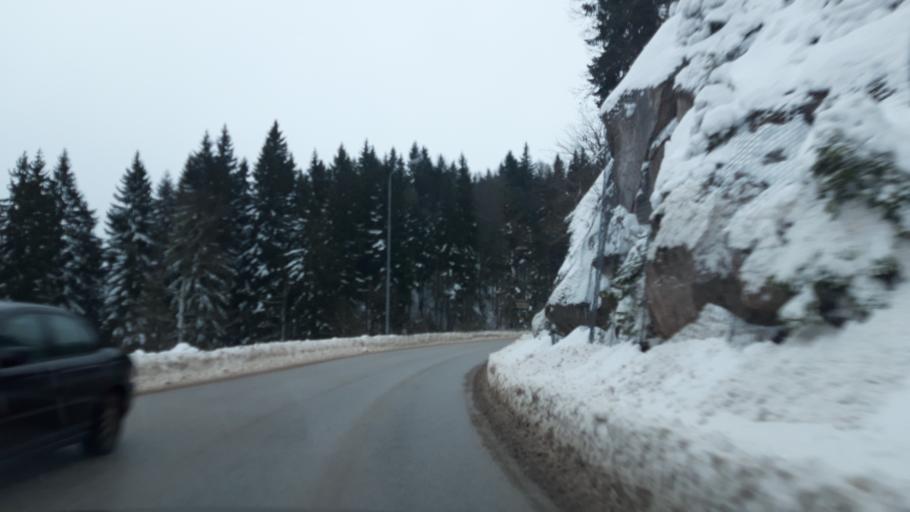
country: BA
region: Republika Srpska
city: Koran
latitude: 43.7418
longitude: 18.5684
